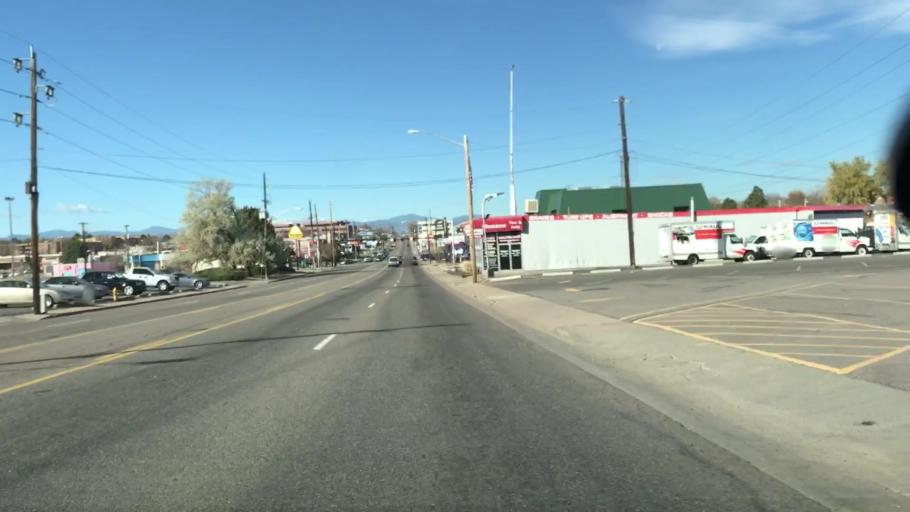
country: US
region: Colorado
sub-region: Arapahoe County
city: Glendale
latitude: 39.6785
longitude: -104.9101
